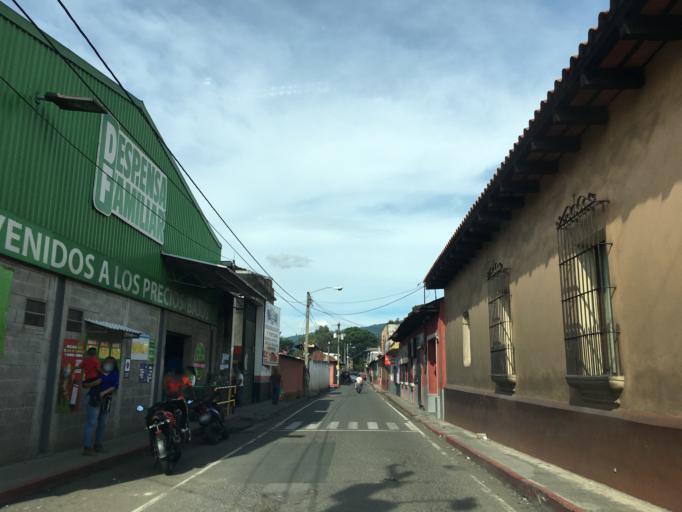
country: GT
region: Sacatepequez
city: Ciudad Vieja
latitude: 14.5253
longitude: -90.7642
